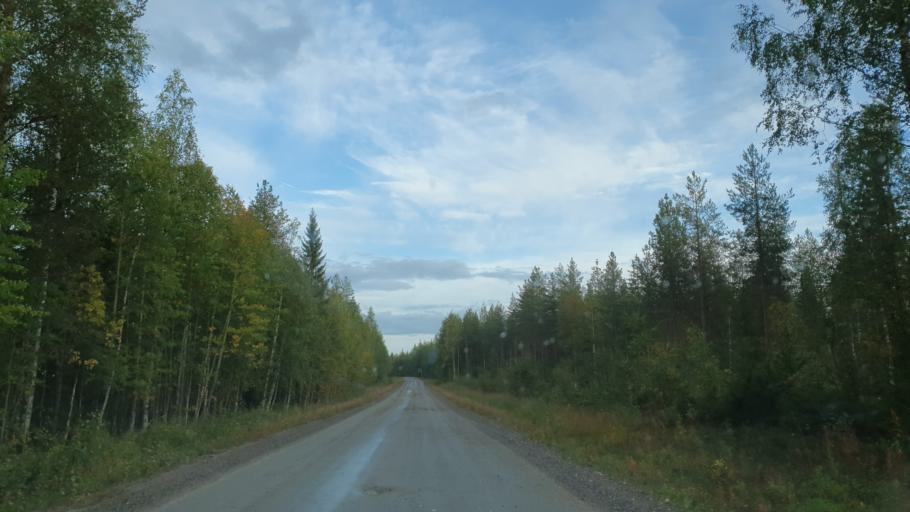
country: FI
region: Kainuu
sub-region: Kehys-Kainuu
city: Kuhmo
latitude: 64.4173
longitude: 29.5013
